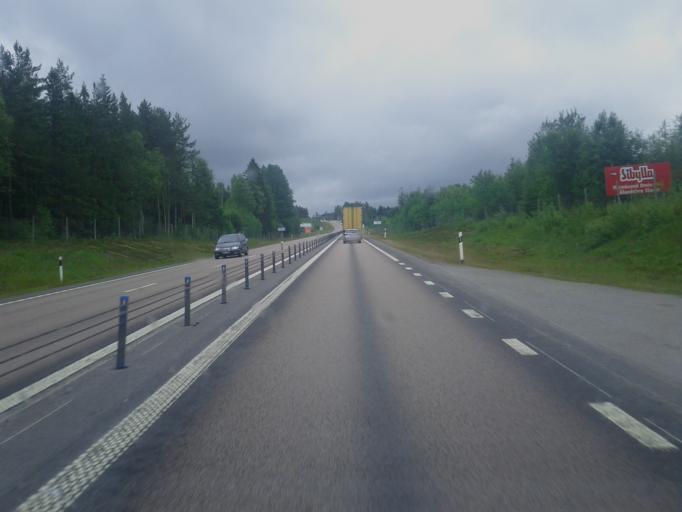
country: SE
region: Vaesternorrland
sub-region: Haernoesands Kommun
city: Haernoesand
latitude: 62.5934
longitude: 17.7985
